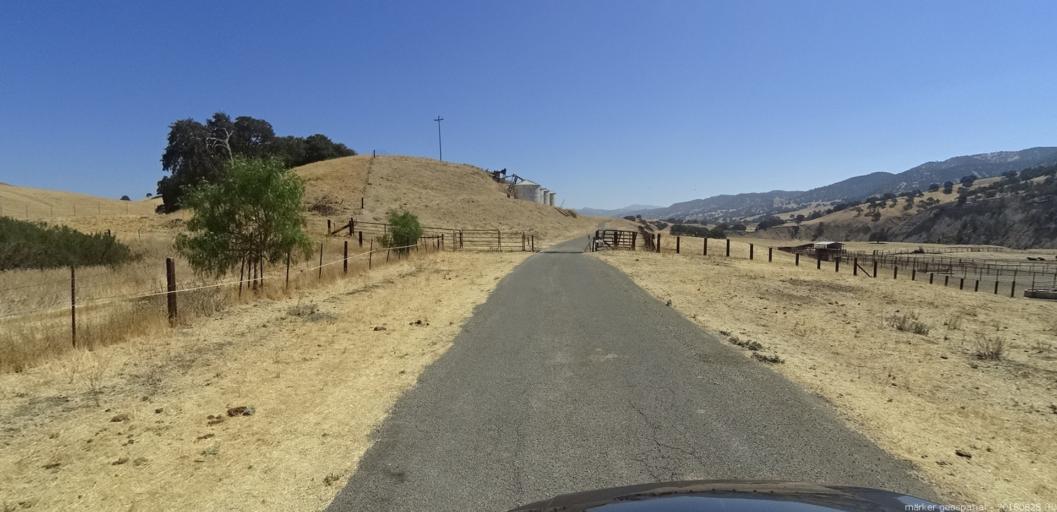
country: US
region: California
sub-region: San Luis Obispo County
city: San Miguel
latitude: 36.0676
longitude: -120.7843
